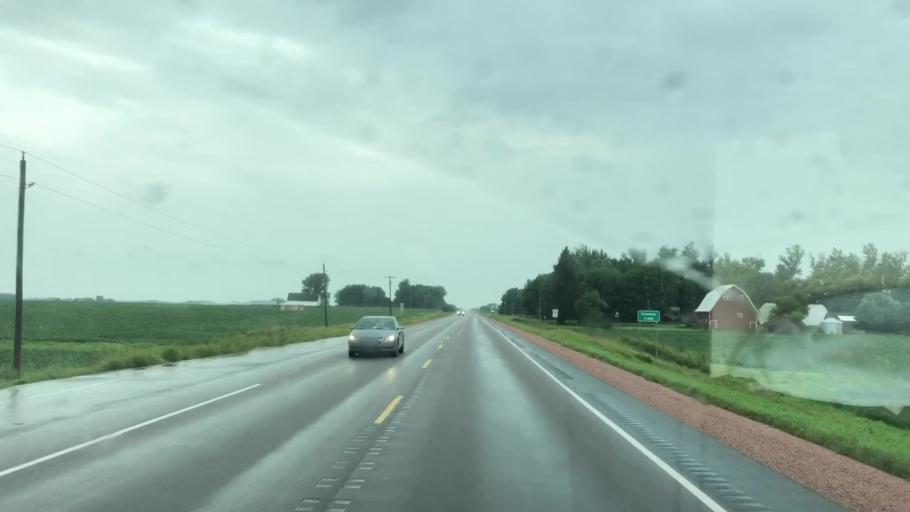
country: US
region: Iowa
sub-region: O'Brien County
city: Sanborn
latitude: 43.1862
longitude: -95.7430
